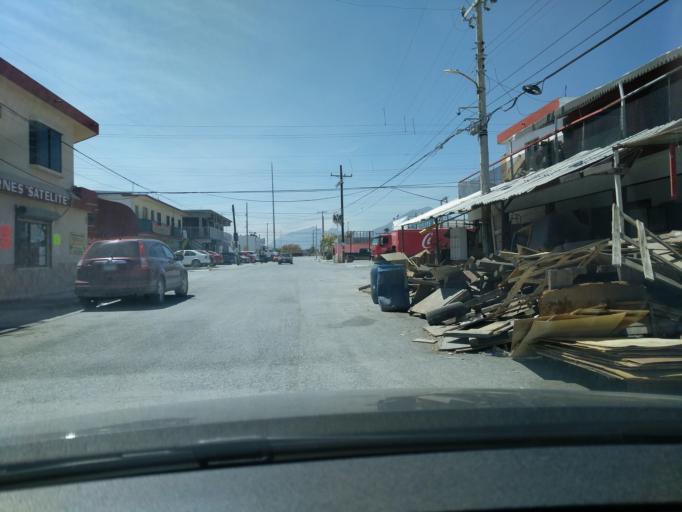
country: MX
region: Nuevo Leon
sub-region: Salinas Victoria
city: Emiliano Zapata
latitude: 25.9126
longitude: -100.2658
